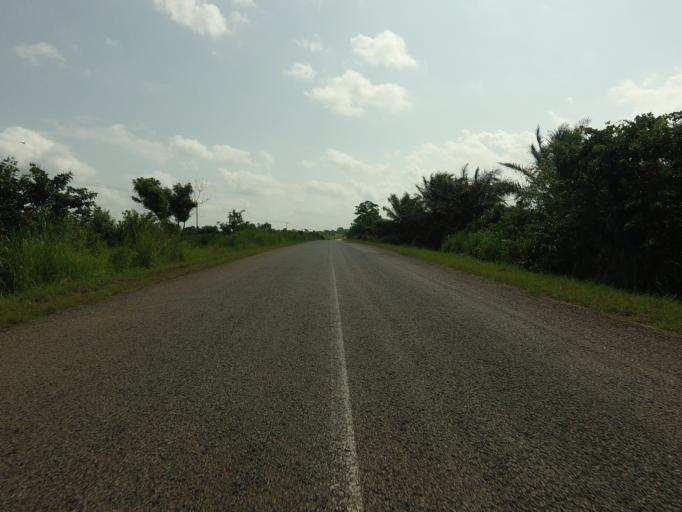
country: GH
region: Volta
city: Ho
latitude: 6.3939
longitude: 0.8062
